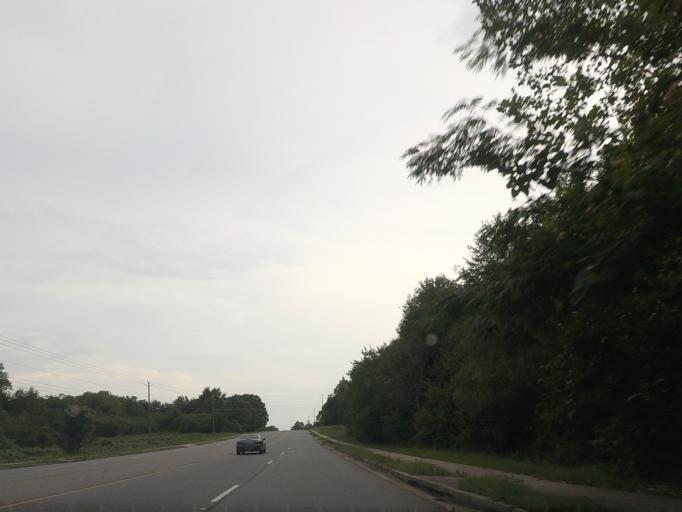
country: US
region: Georgia
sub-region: Houston County
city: Centerville
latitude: 32.7289
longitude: -83.6823
